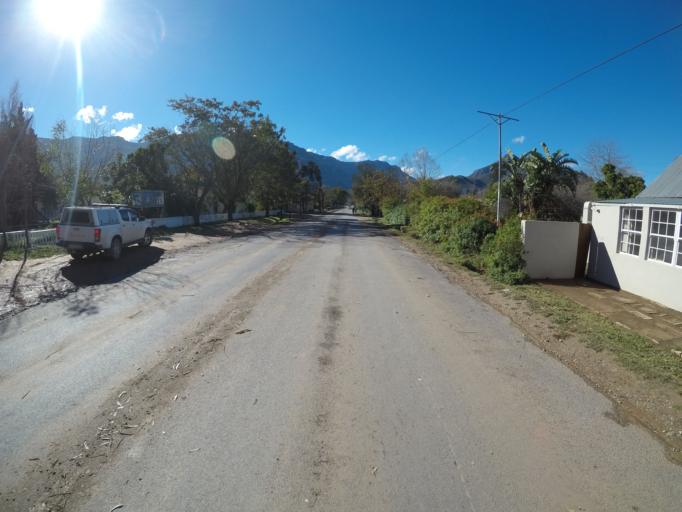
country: ZA
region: Western Cape
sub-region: Overberg District Municipality
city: Caledon
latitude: -34.0534
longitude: 19.6039
